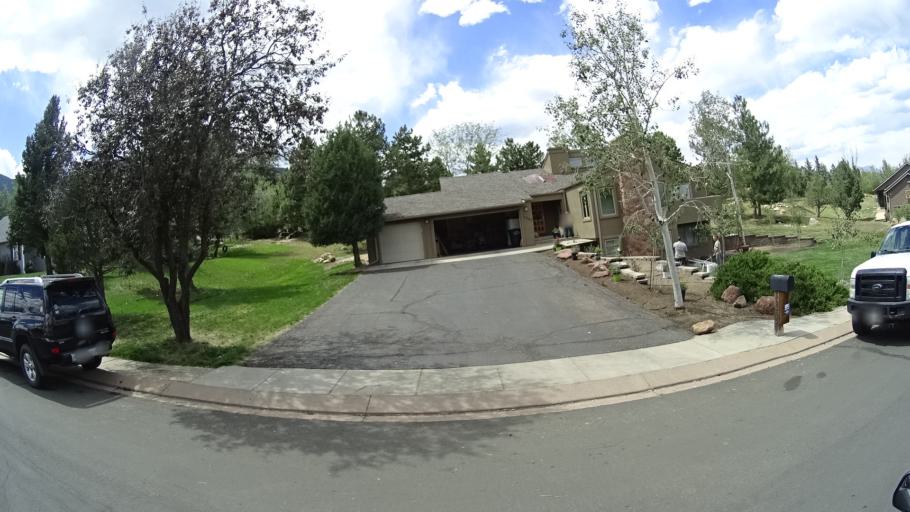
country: US
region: Colorado
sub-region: El Paso County
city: Stratmoor
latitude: 38.7740
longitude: -104.8313
